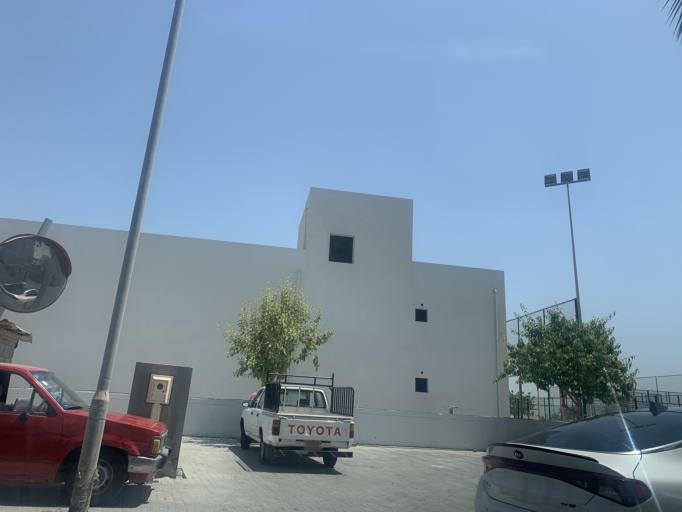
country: BH
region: Muharraq
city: Al Muharraq
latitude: 26.2827
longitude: 50.6208
